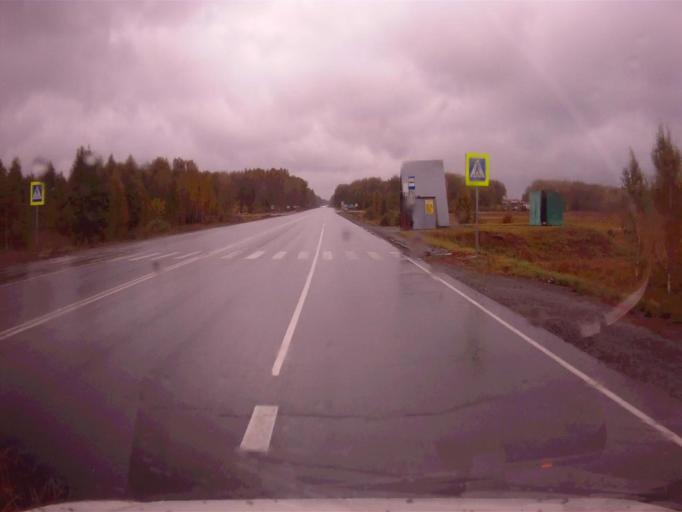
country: RU
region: Chelyabinsk
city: Argayash
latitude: 55.4567
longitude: 60.9268
